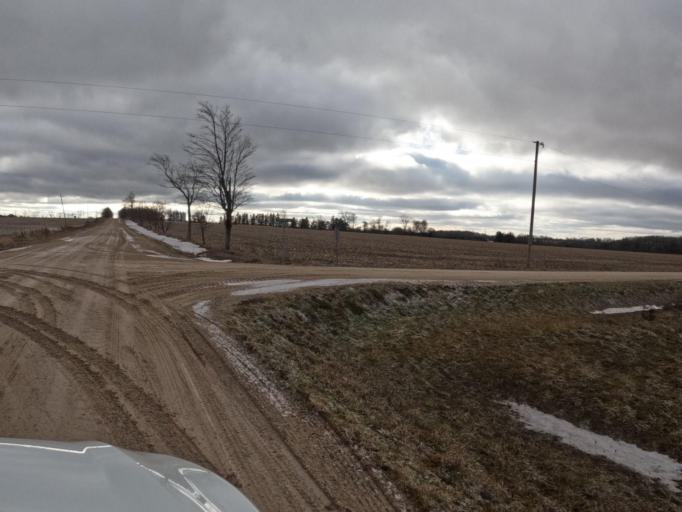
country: CA
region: Ontario
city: Shelburne
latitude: 44.0157
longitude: -80.3679
